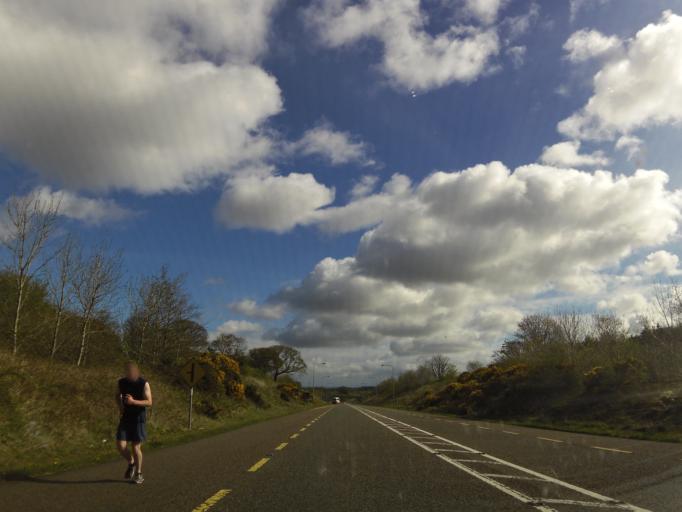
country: IE
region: Connaught
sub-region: Maigh Eo
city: Kiltamagh
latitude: 53.7939
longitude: -8.9289
